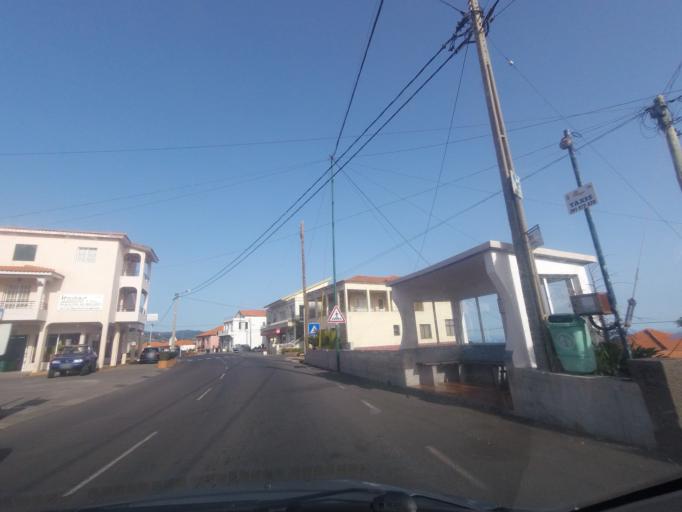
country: PT
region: Madeira
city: Ponta do Sol
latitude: 32.6972
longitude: -17.1180
